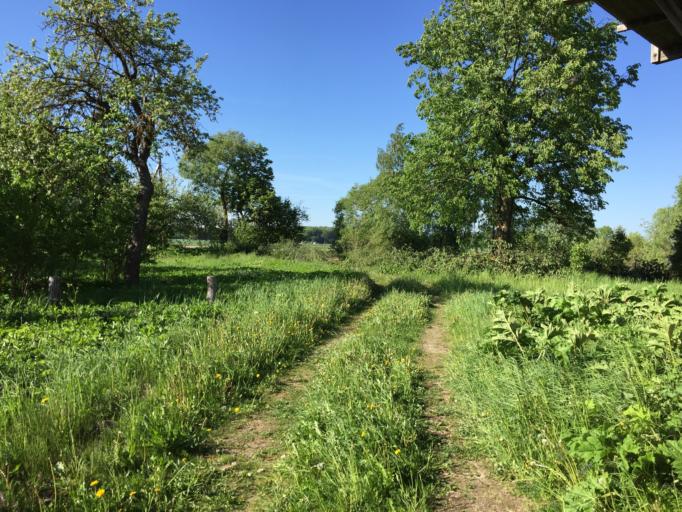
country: LV
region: Jelgava
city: Jelgava
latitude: 56.5407
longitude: 23.7166
